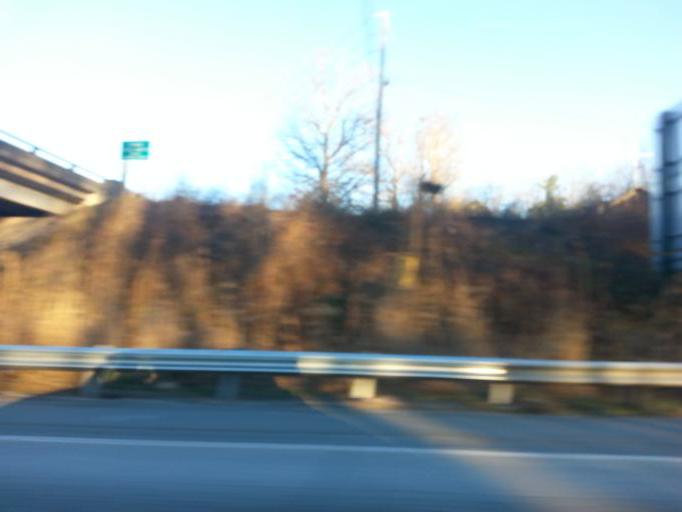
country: US
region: North Carolina
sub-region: Henderson County
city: Fletcher
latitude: 35.4320
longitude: -82.5305
